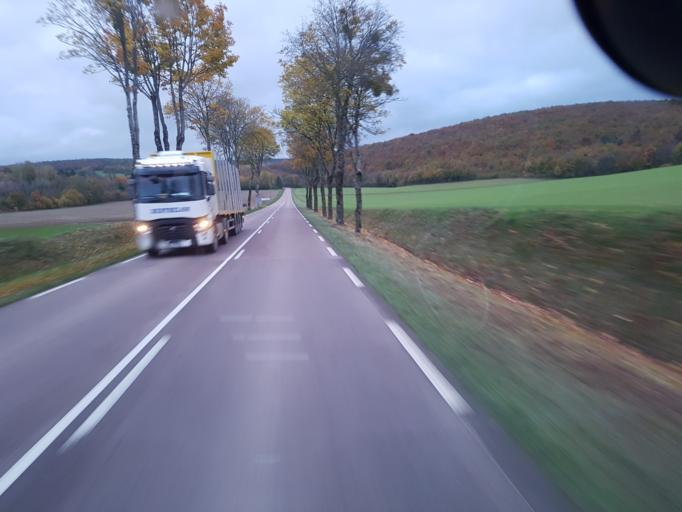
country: FR
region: Champagne-Ardenne
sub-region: Departement de l'Aube
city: Mussy-sur-Seine
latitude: 48.0031
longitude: 4.4744
